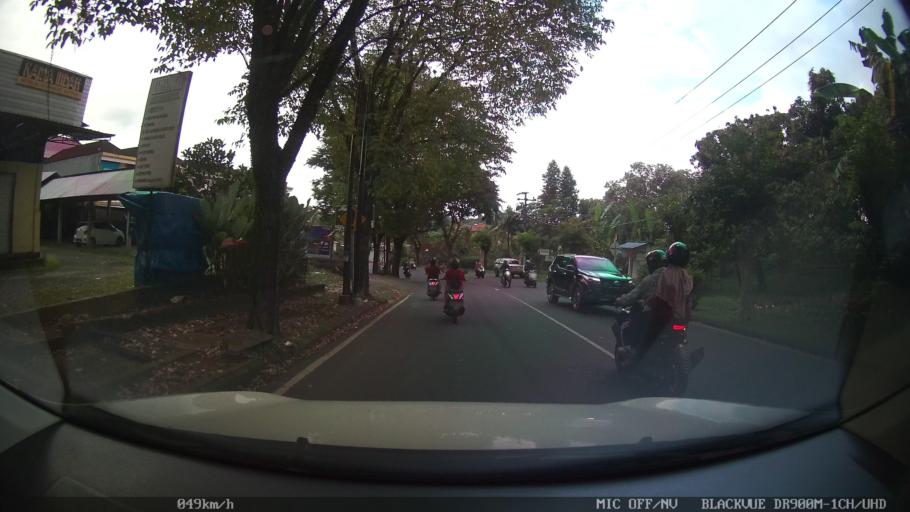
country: ID
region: Bali
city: Banjar Tegal Belodan
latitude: -8.5368
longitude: 115.1152
